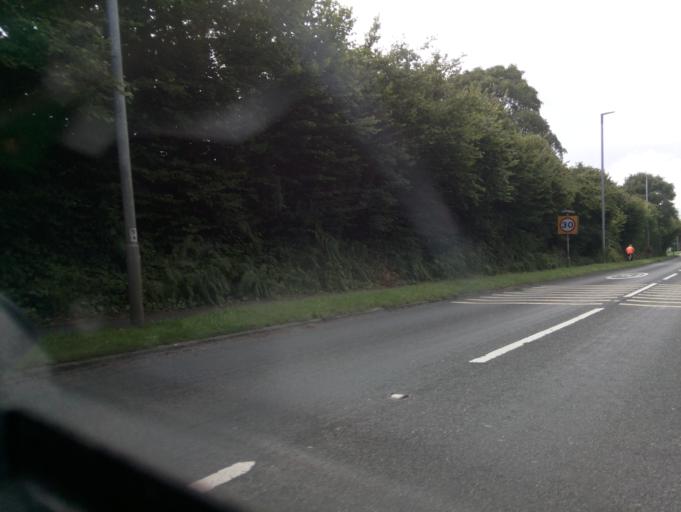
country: GB
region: England
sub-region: Somerset
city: Yeovil
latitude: 50.9279
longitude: -2.6385
